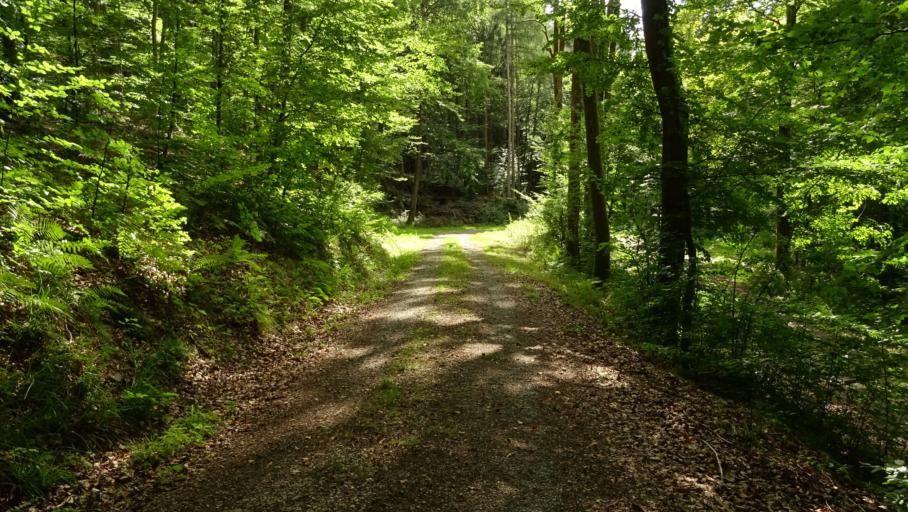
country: DE
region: Baden-Wuerttemberg
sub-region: Karlsruhe Region
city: Neckargerach
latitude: 49.4081
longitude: 9.0992
